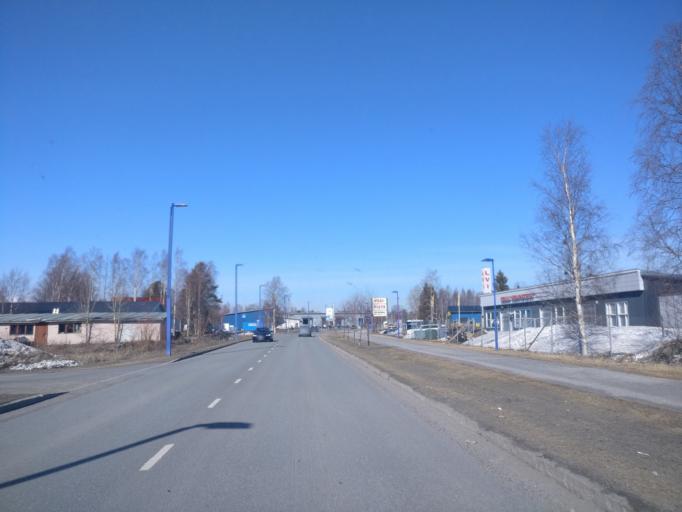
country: FI
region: Lapland
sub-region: Kemi-Tornio
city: Kemi
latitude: 65.7390
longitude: 24.5784
